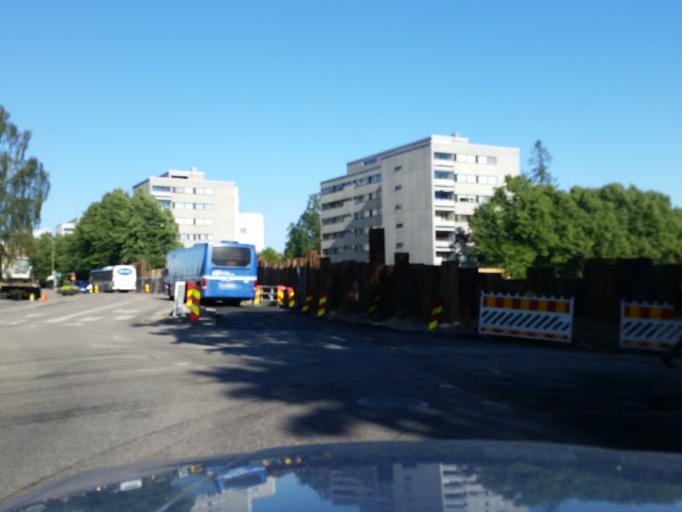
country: FI
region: Uusimaa
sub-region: Helsinki
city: Teekkarikylae
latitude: 60.1604
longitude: 24.8802
